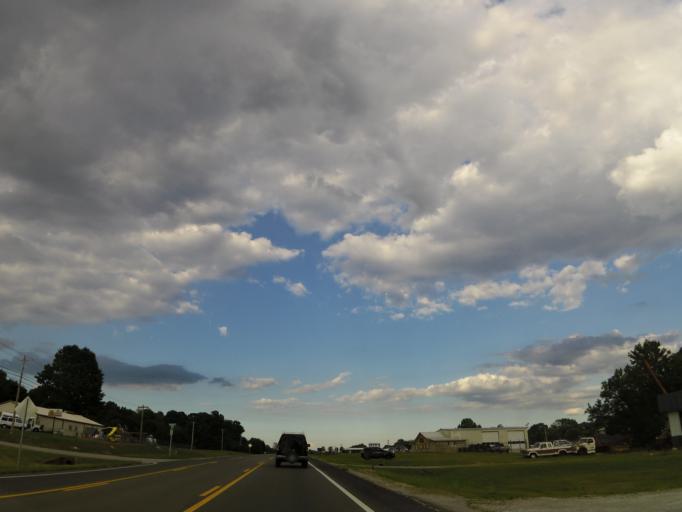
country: US
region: Tennessee
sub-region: Maury County
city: Columbia
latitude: 35.6362
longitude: -87.0031
